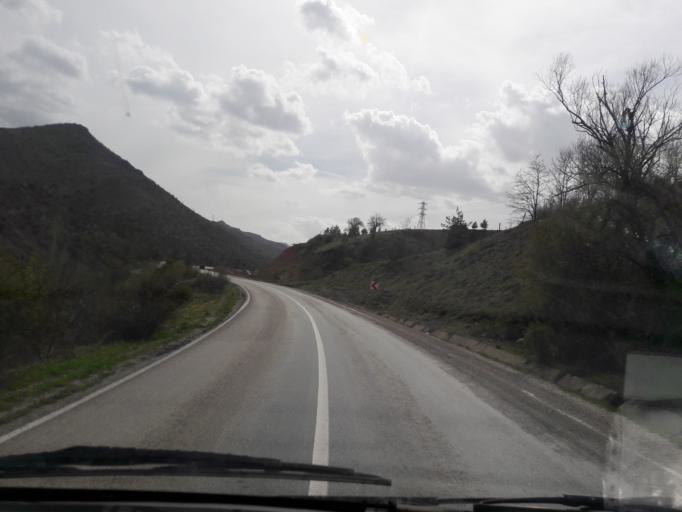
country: TR
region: Gumushane
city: Kale
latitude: 40.3498
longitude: 39.5523
